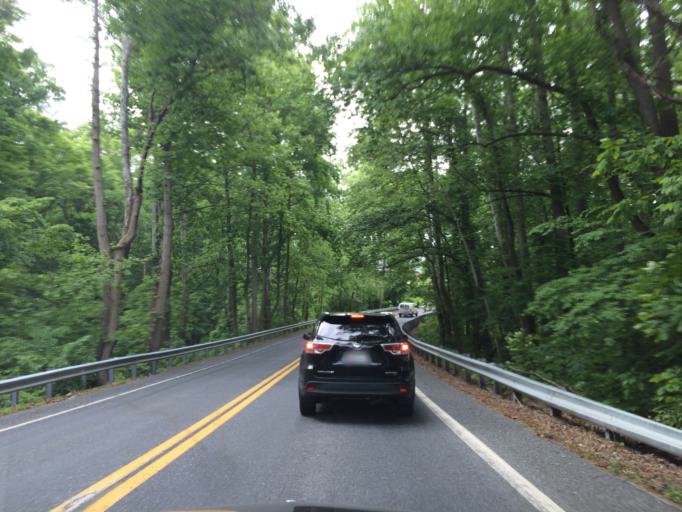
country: US
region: Maryland
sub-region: Howard County
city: Columbia
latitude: 39.2394
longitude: -76.9055
